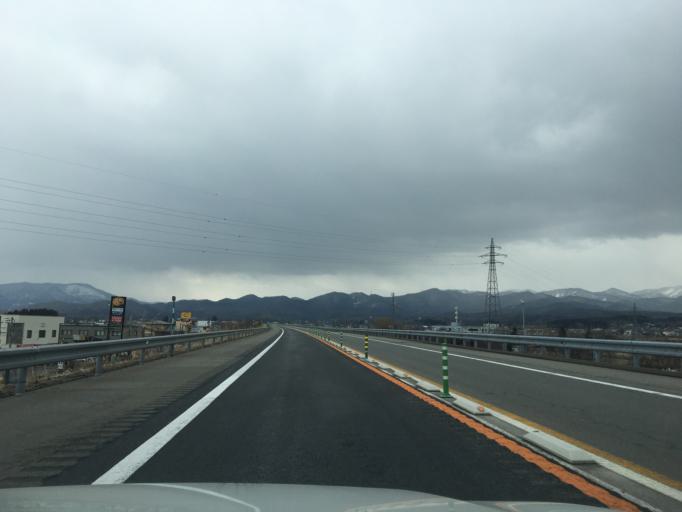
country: JP
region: Aomori
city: Aomori Shi
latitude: 40.7951
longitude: 140.7663
